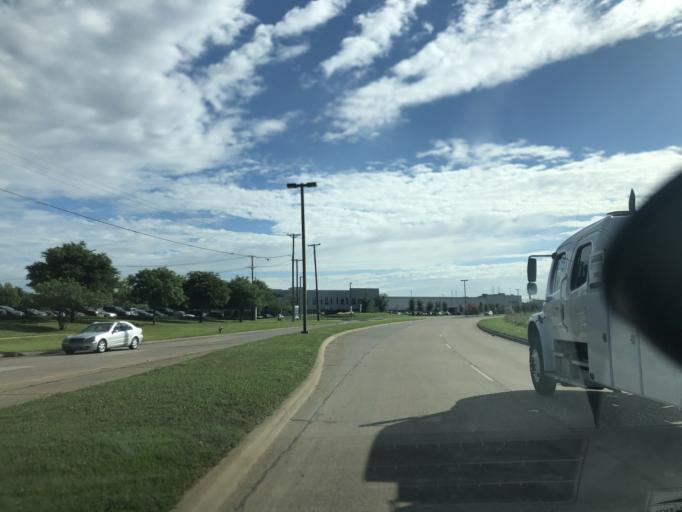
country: US
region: Texas
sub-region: Tarrant County
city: Euless
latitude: 32.8278
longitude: -97.0297
